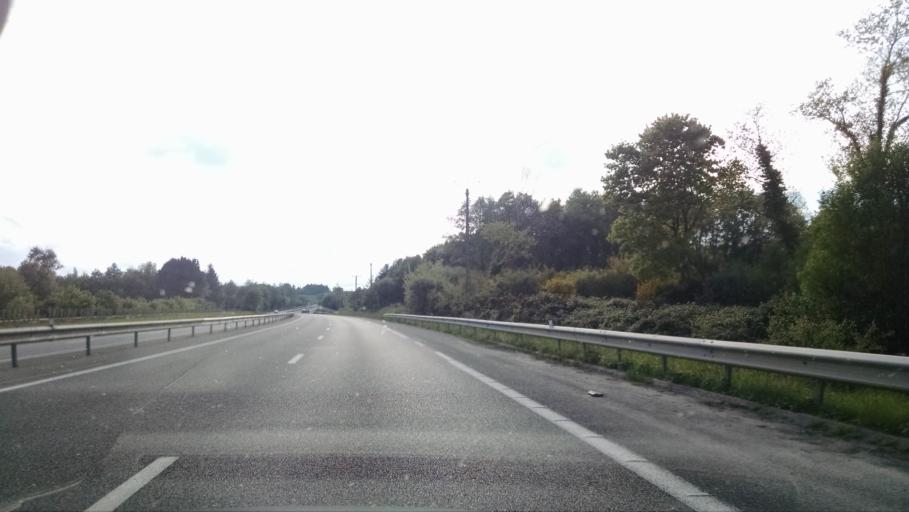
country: FR
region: Brittany
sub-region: Departement du Finistere
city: Guerlesquin
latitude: 48.5676
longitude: -3.5597
